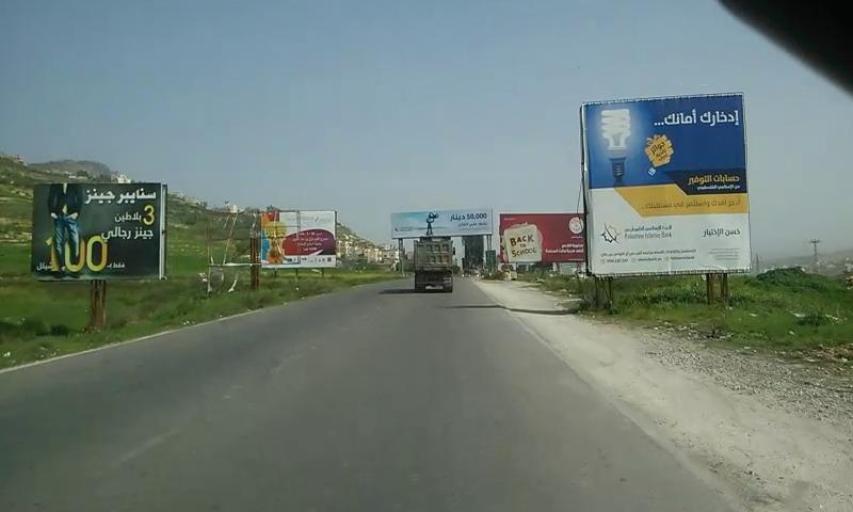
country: PS
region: West Bank
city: Kafr Qallil
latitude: 32.1797
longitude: 35.2746
